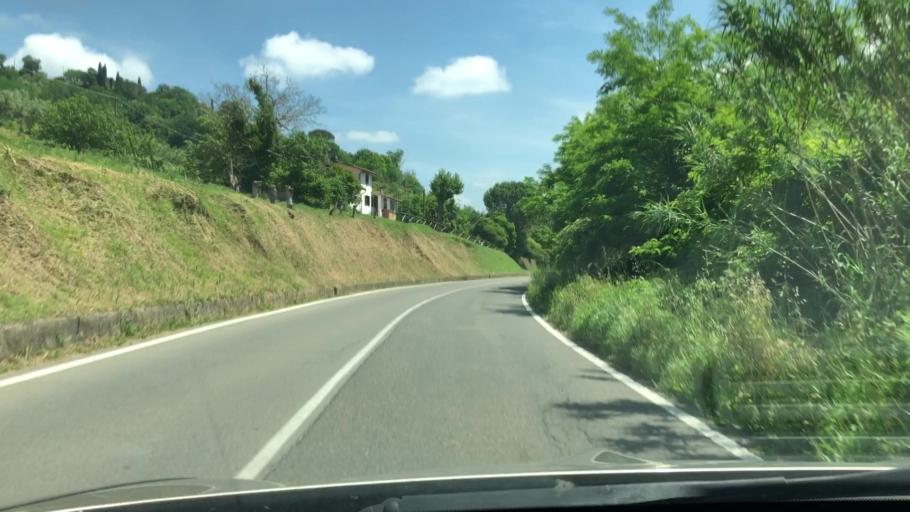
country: IT
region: Tuscany
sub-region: Province of Pisa
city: Forcoli
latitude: 43.6079
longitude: 10.6941
